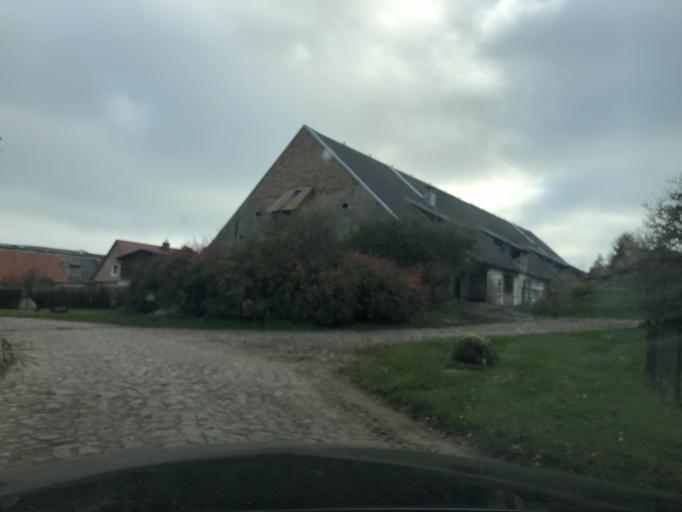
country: DE
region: Mecklenburg-Vorpommern
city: Kessin
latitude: 53.7444
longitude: 13.3482
